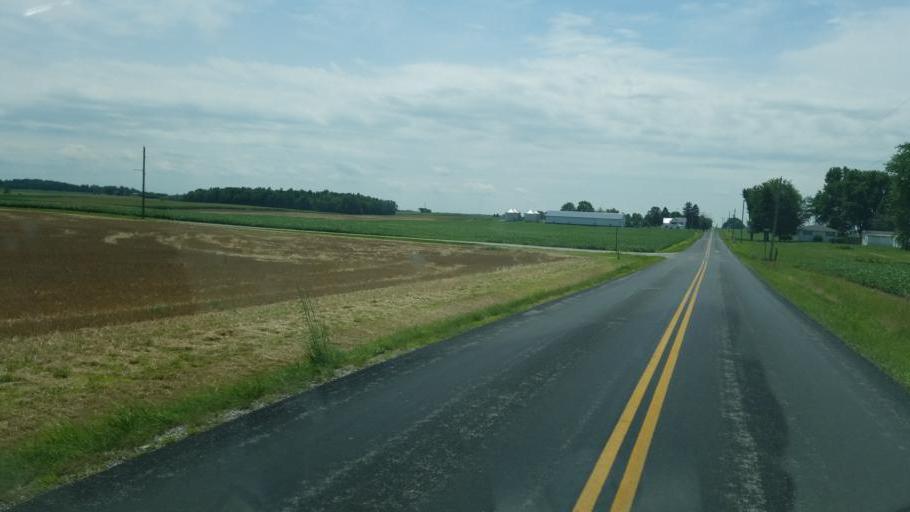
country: US
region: Ohio
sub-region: Crawford County
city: Bucyrus
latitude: 40.8715
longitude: -82.9018
